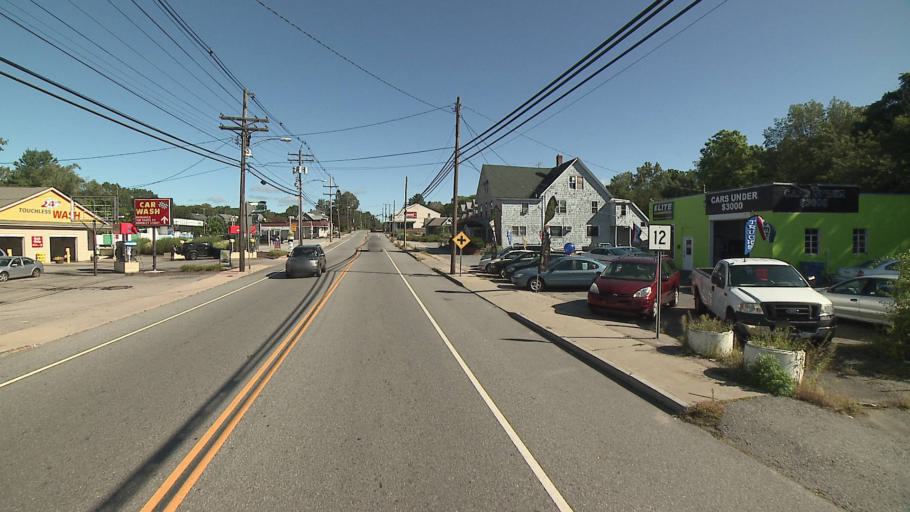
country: US
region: Connecticut
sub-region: New London County
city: Norwich
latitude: 41.5445
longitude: -72.0546
